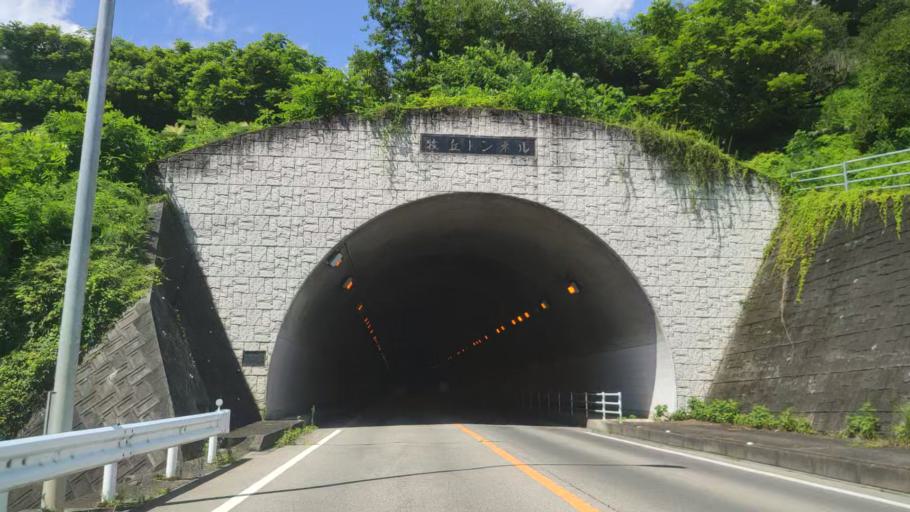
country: JP
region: Yamanashi
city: Enzan
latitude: 35.7434
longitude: 138.7080
